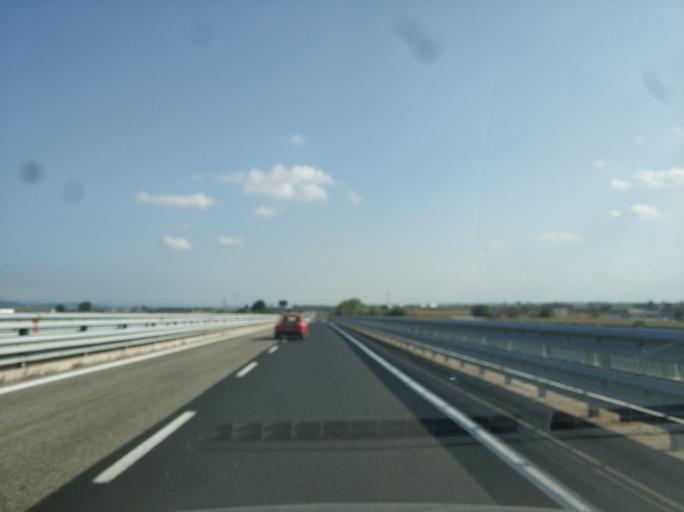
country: IT
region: Piedmont
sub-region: Provincia di Cuneo
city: Roreto
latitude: 44.6911
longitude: 7.8266
